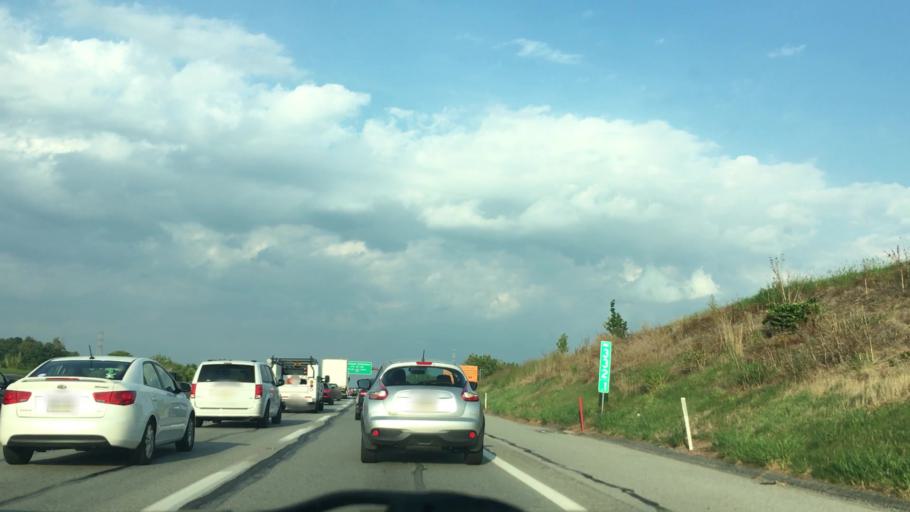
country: US
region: Pennsylvania
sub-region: Montgomery County
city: Conshohocken
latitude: 40.1064
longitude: -75.3096
